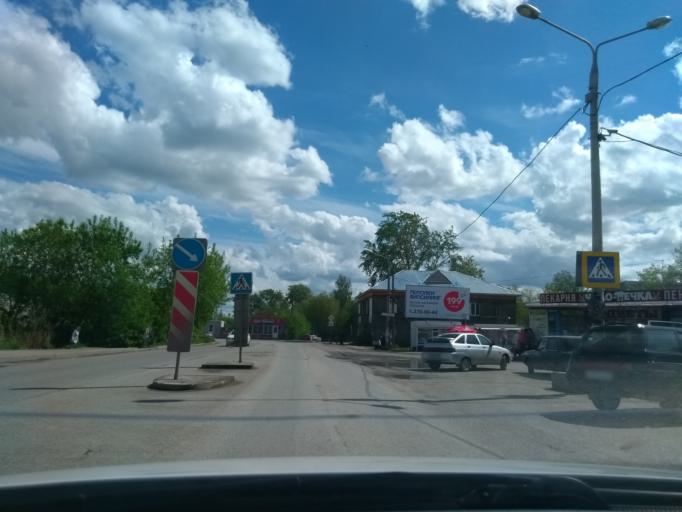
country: RU
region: Perm
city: Kondratovo
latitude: 58.0056
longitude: 56.1175
